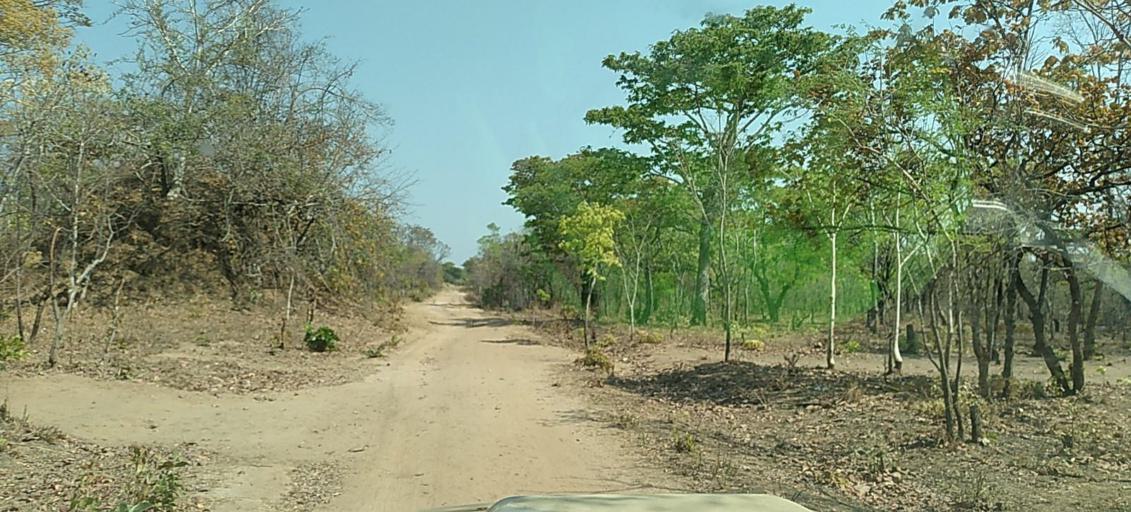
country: ZM
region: North-Western
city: Kalengwa
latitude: -13.2976
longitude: 24.7921
